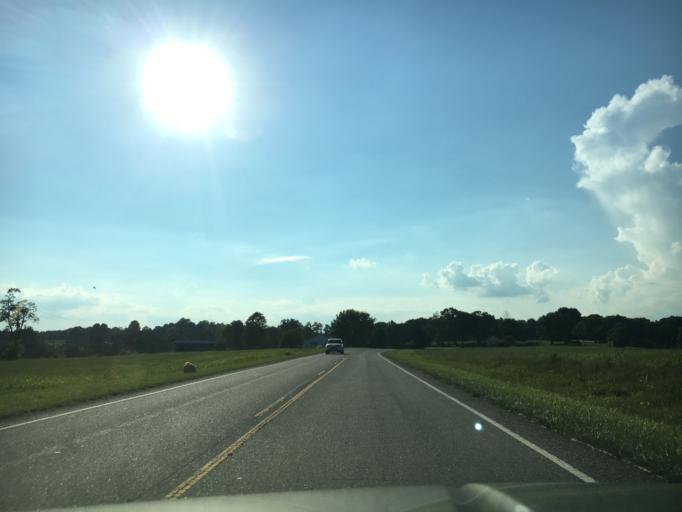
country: US
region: Virginia
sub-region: City of Bedford
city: Bedford
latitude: 37.2283
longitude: -79.5267
